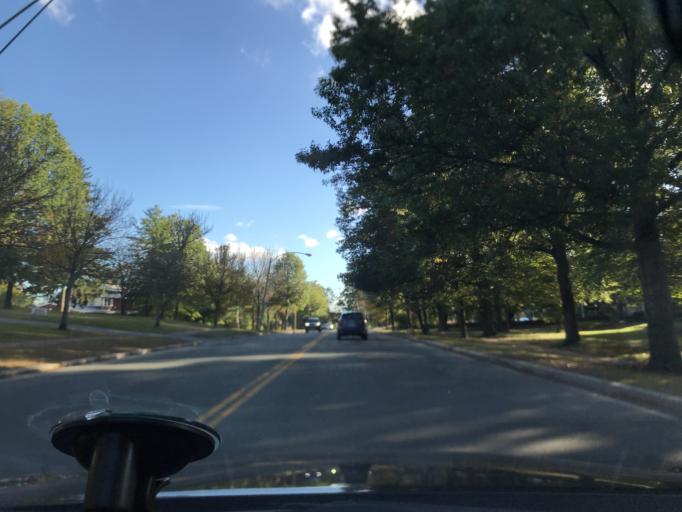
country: US
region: Massachusetts
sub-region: Suffolk County
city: Jamaica Plain
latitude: 42.2915
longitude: -71.1469
